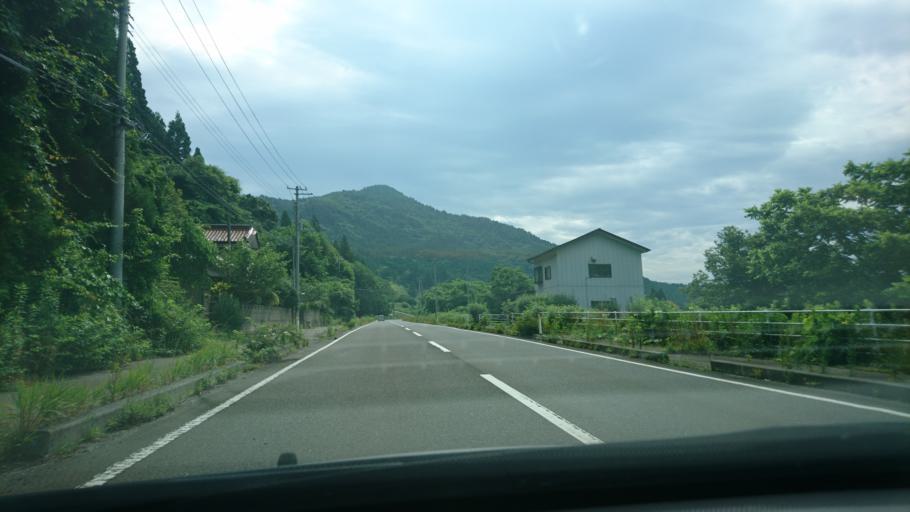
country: JP
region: Iwate
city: Ofunato
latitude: 38.8108
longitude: 141.4803
